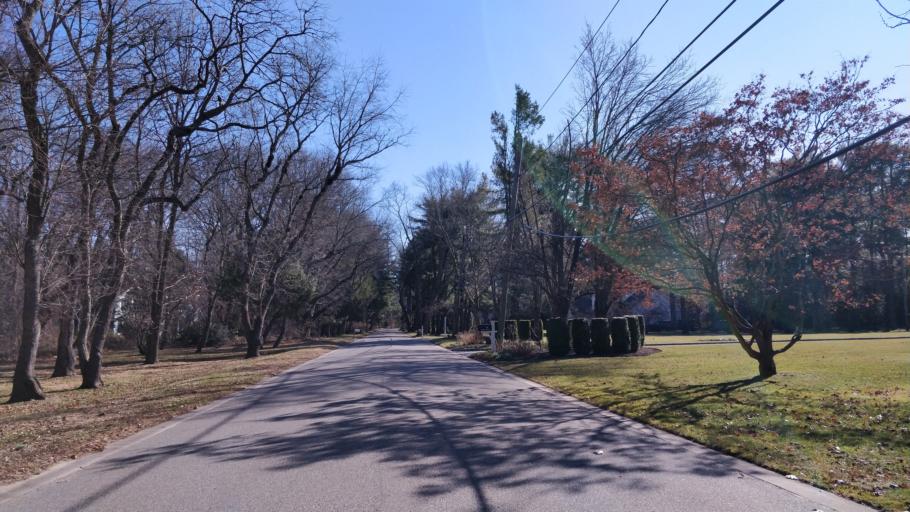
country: US
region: New York
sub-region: Nassau County
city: Upper Brookville
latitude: 40.8492
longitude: -73.5606
